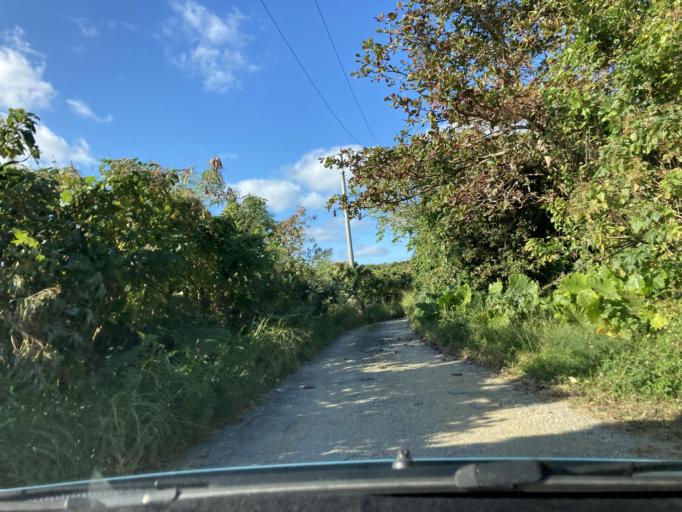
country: JP
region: Okinawa
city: Katsuren-haebaru
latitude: 26.3153
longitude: 127.9284
